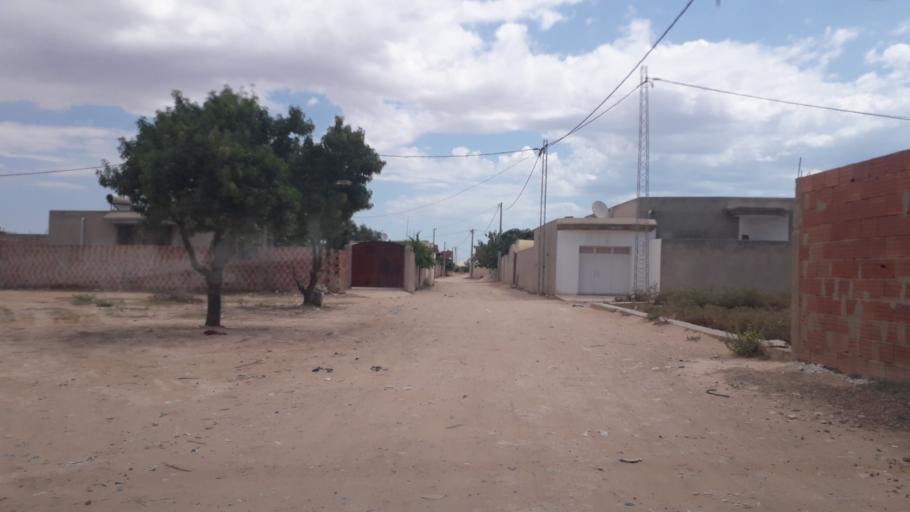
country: TN
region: Safaqis
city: Al Qarmadah
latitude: 34.8384
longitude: 10.7755
